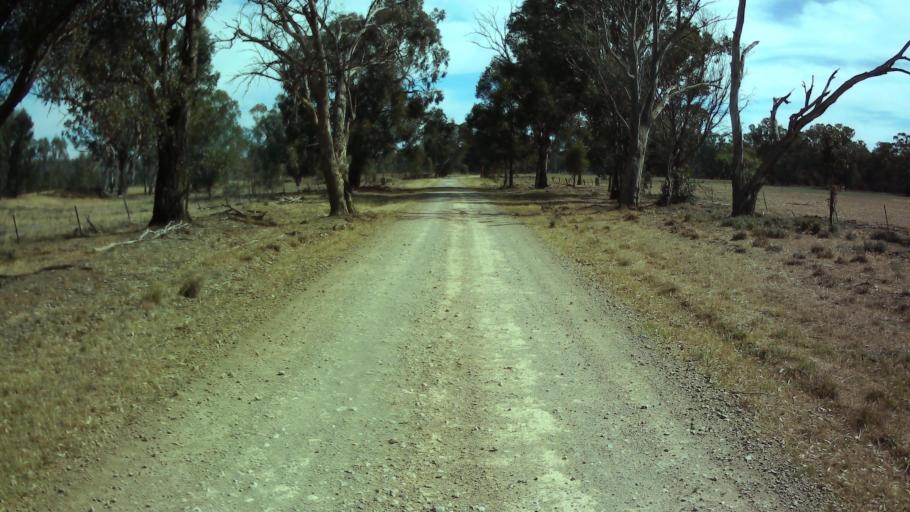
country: AU
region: New South Wales
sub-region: Weddin
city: Grenfell
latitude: -33.6932
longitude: 148.3035
